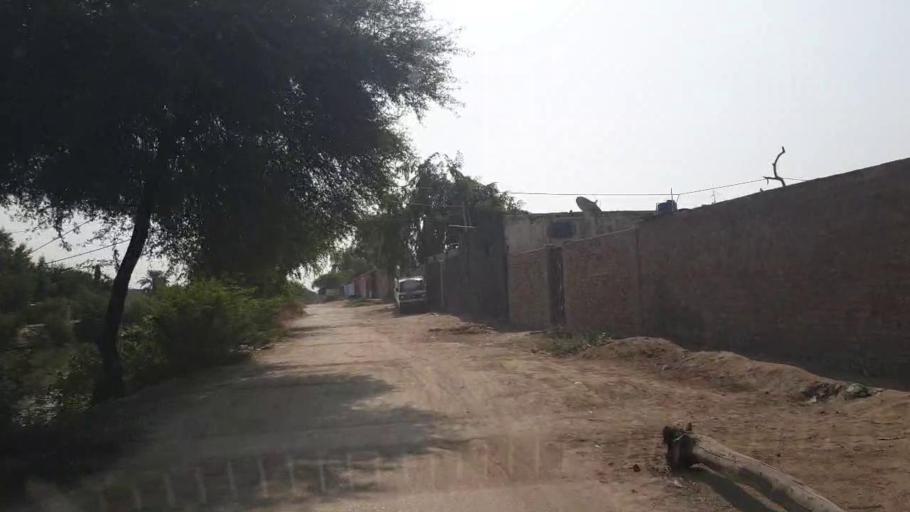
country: PK
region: Sindh
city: Badin
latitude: 24.6525
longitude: 68.8437
